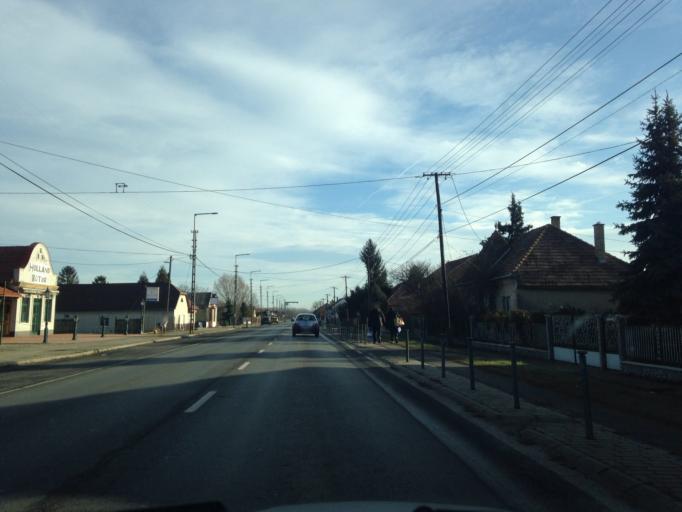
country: HU
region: Gyor-Moson-Sopron
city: Abda
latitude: 47.6952
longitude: 17.5466
